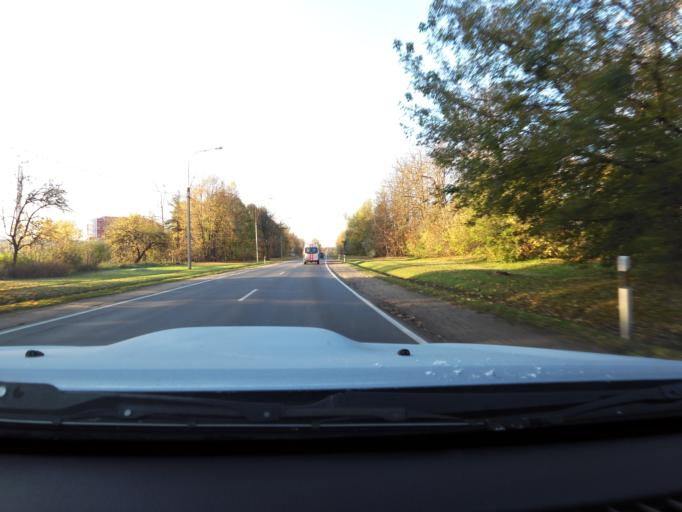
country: LT
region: Vilnius County
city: Vilkpede
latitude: 54.6413
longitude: 25.2614
